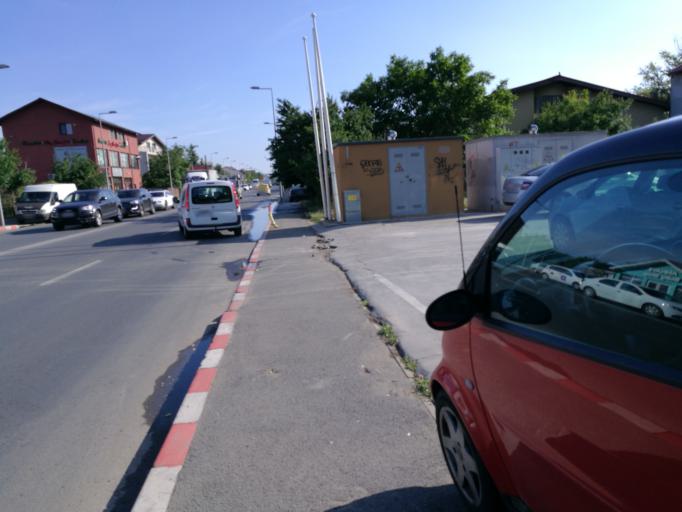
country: RO
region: Ilfov
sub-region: Voluntari City
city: Voluntari
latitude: 44.5068
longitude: 26.1373
